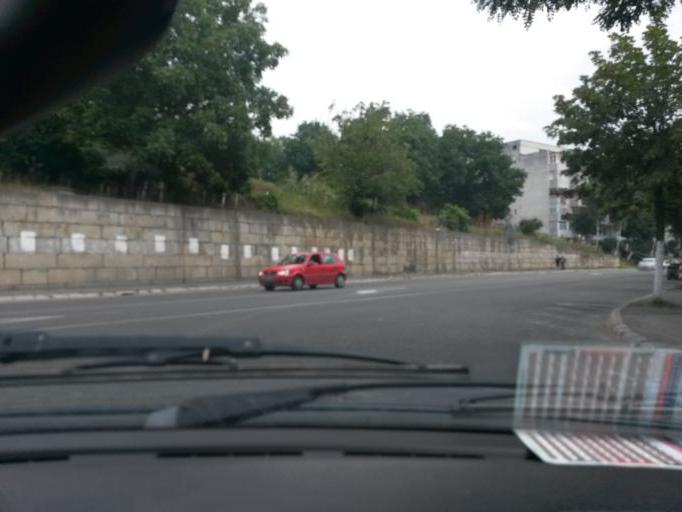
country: RO
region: Mures
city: Targu-Mures
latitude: 46.5396
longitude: 24.5849
